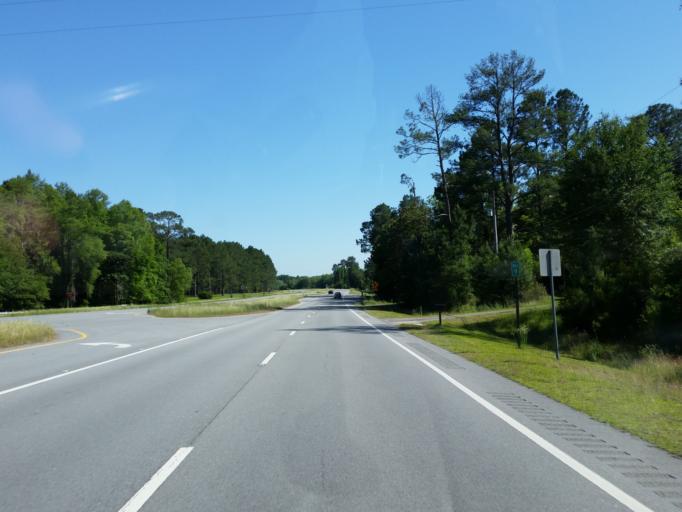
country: US
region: Georgia
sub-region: Lowndes County
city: Valdosta
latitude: 30.7362
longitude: -83.2206
